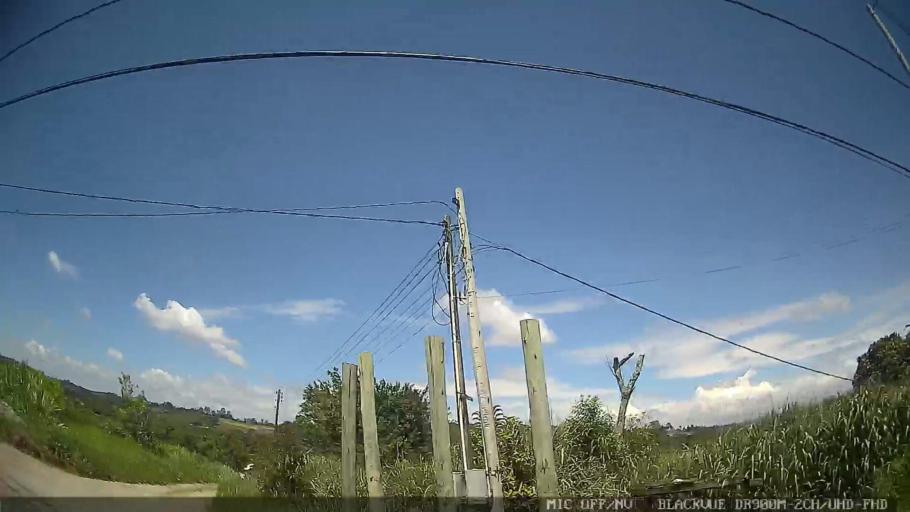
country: BR
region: Sao Paulo
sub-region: Biritiba-Mirim
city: Biritiba Mirim
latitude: -23.5719
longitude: -46.0827
